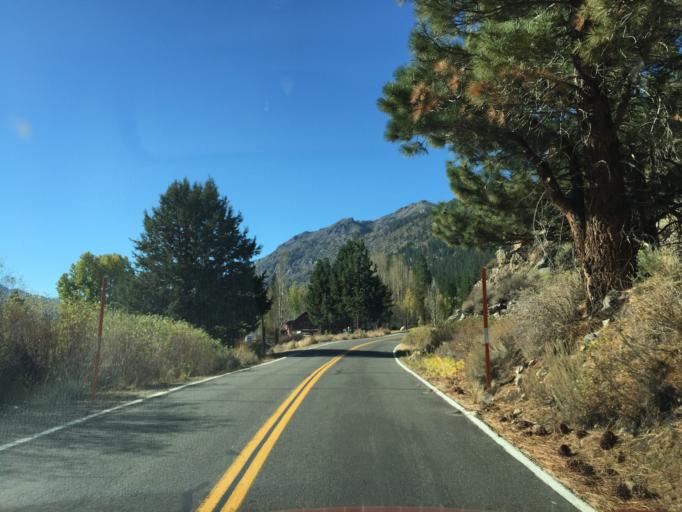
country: US
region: California
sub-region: Mono County
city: Bridgeport
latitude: 38.3263
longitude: -119.5527
